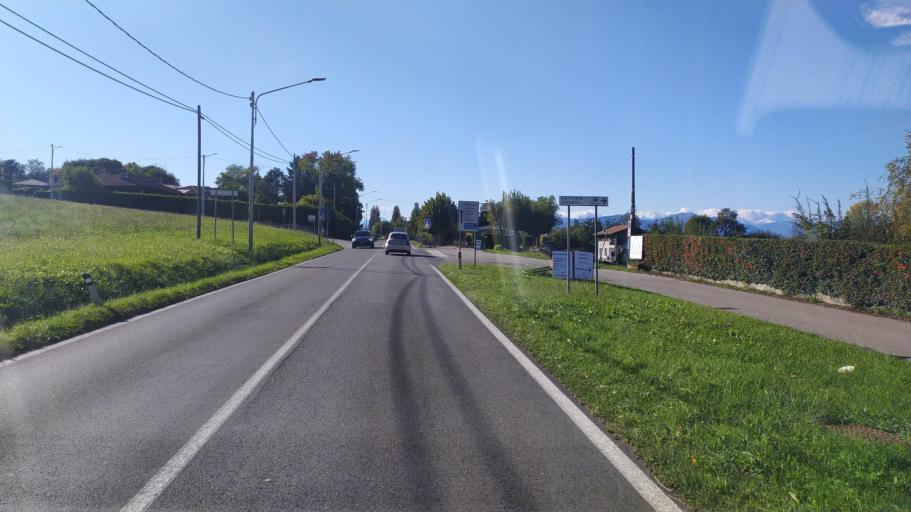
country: IT
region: Lombardy
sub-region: Provincia di Varese
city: Bodio
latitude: 45.7904
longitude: 8.7605
